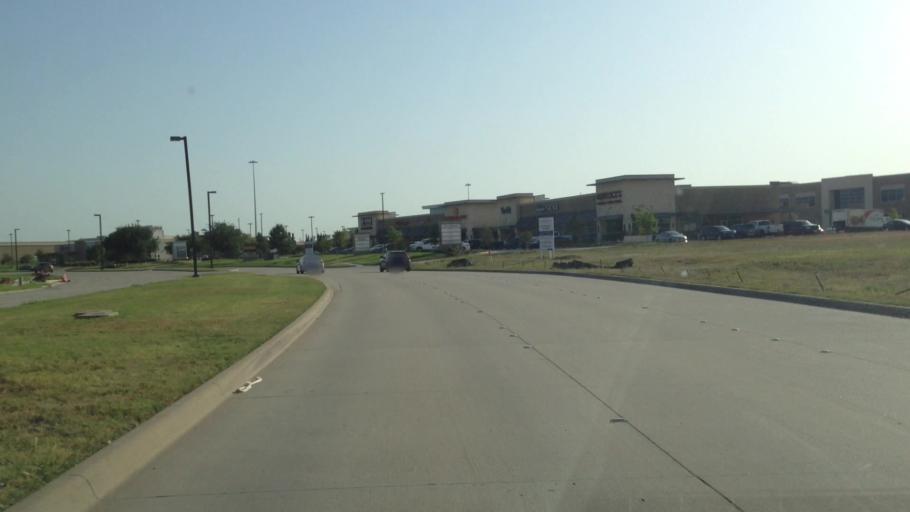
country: US
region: Texas
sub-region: Collin County
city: Frisco
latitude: 33.0897
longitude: -96.8144
